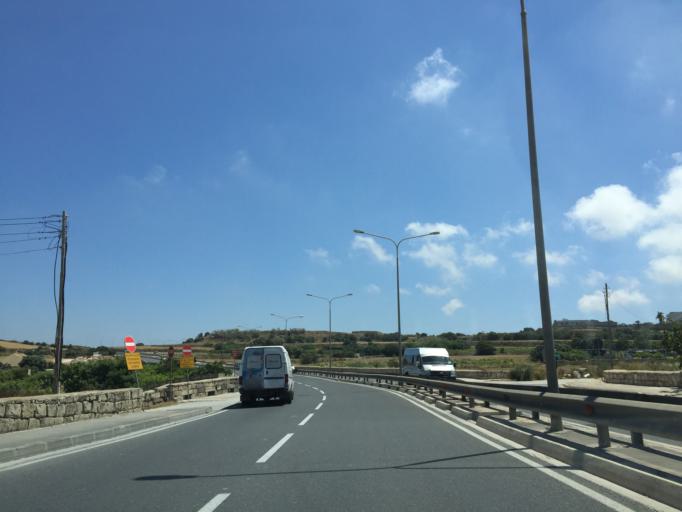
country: MT
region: L-Imdina
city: Imdina
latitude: 35.8887
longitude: 14.4101
